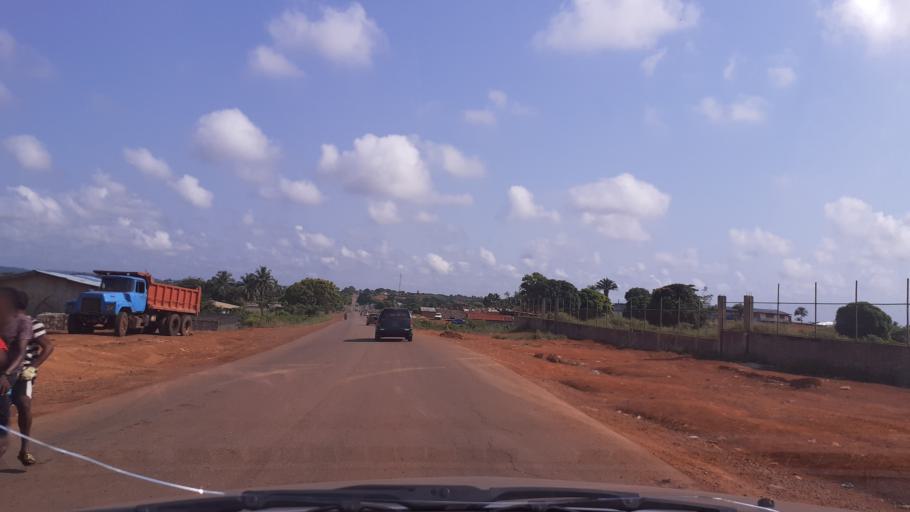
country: LR
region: Montserrado
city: Bensonville City
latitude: 6.2092
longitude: -10.5478
